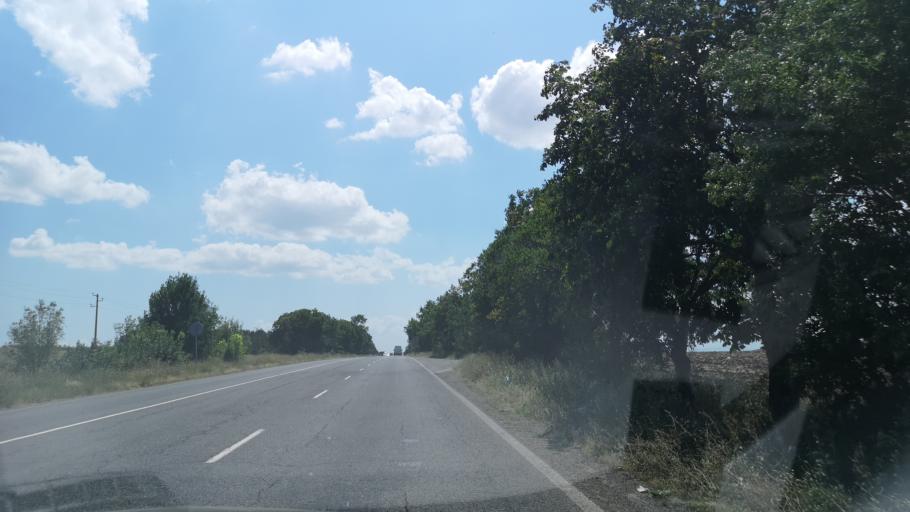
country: BG
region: Burgas
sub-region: Obshtina Kameno
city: Kameno
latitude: 42.6343
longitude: 27.3417
